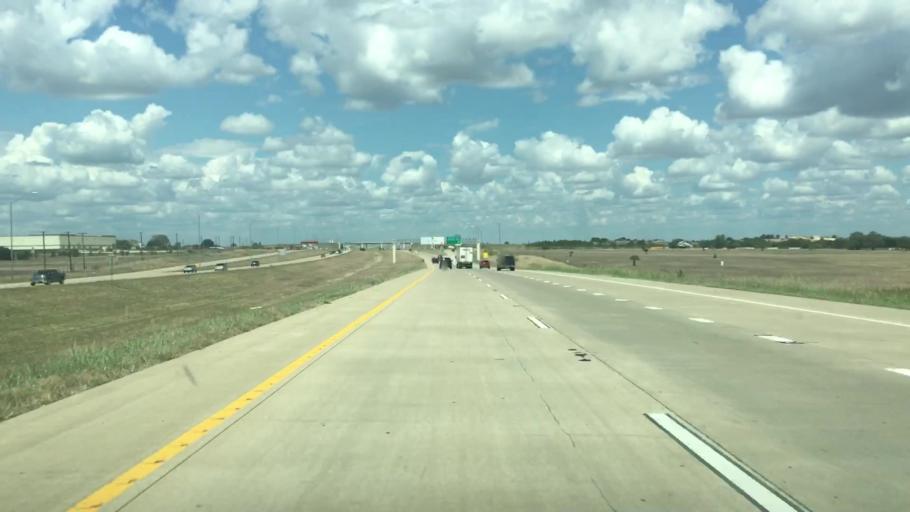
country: US
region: Texas
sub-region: Williamson County
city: Hutto
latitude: 30.5782
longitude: -97.5855
